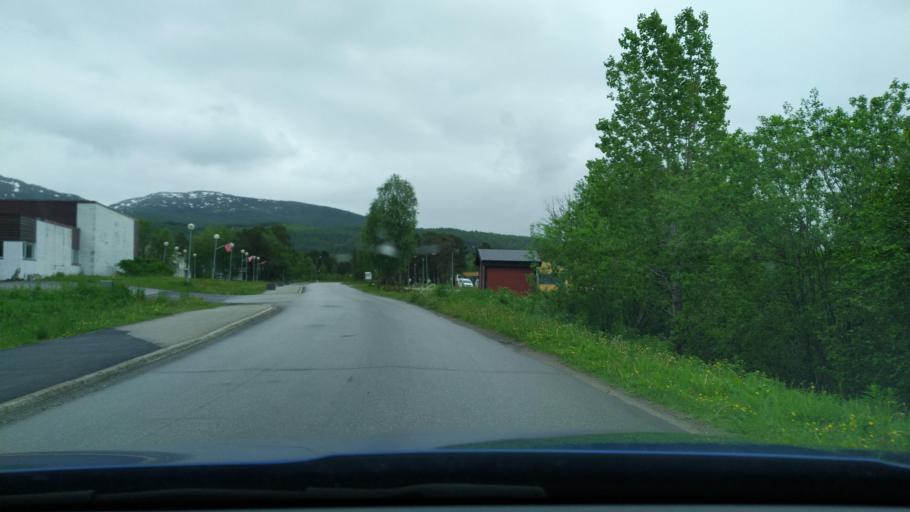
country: NO
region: Troms
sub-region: Dyroy
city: Brostadbotn
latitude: 69.0913
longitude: 17.6963
